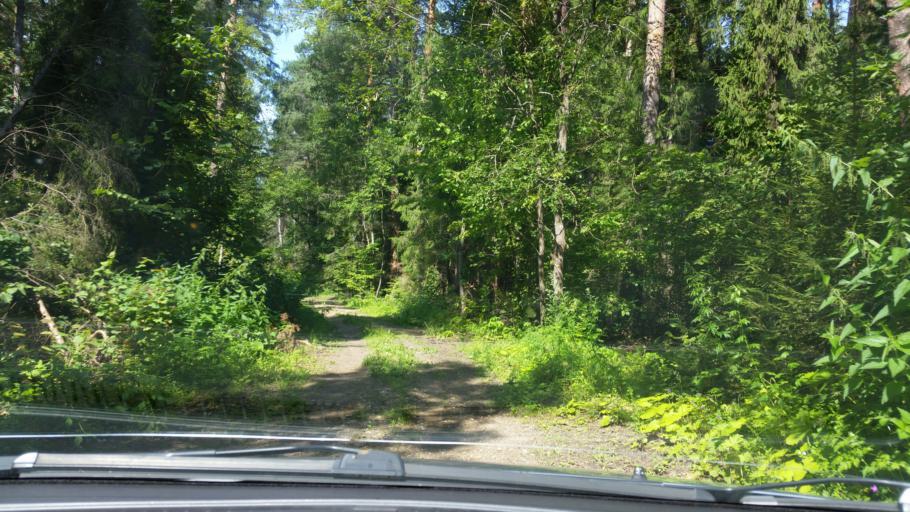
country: RU
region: Moskovskaya
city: Bol'shoye Gryzlovo
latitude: 54.9084
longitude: 37.7594
